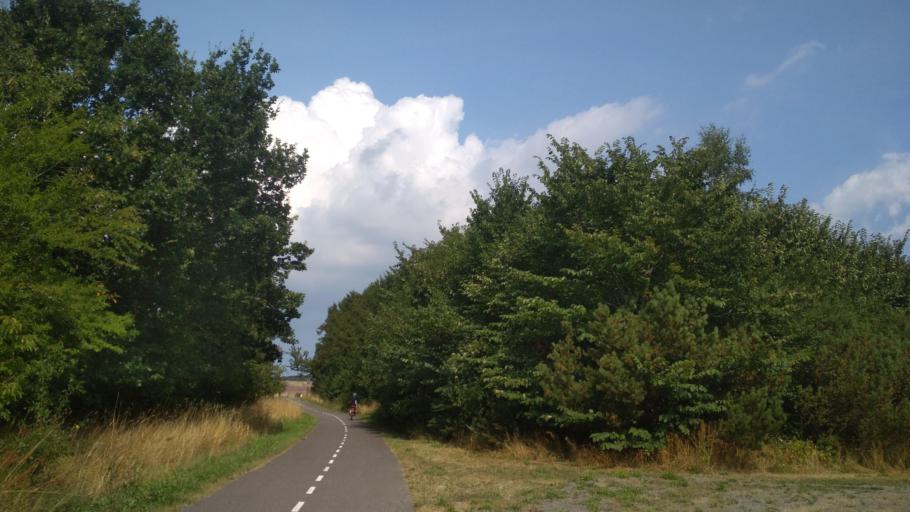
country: DK
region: Capital Region
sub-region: Bornholm Kommune
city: Akirkeby
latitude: 55.0746
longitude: 14.9157
